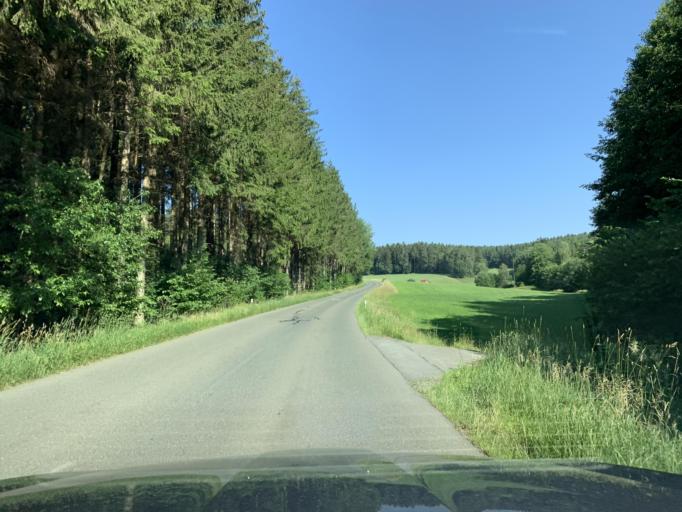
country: DE
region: Bavaria
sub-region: Upper Palatinate
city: Bach
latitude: 49.4059
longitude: 12.3826
